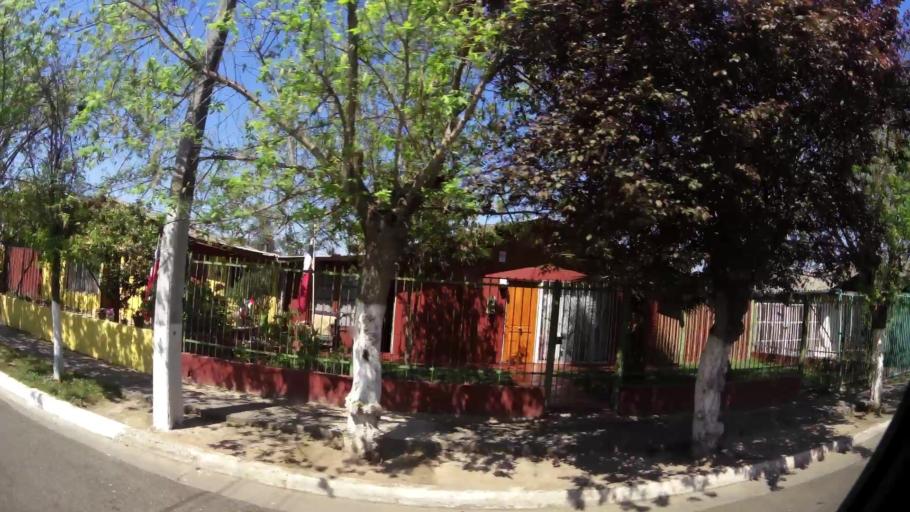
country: CL
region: Santiago Metropolitan
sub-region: Provincia de Talagante
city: Penaflor
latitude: -33.5723
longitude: -70.8087
